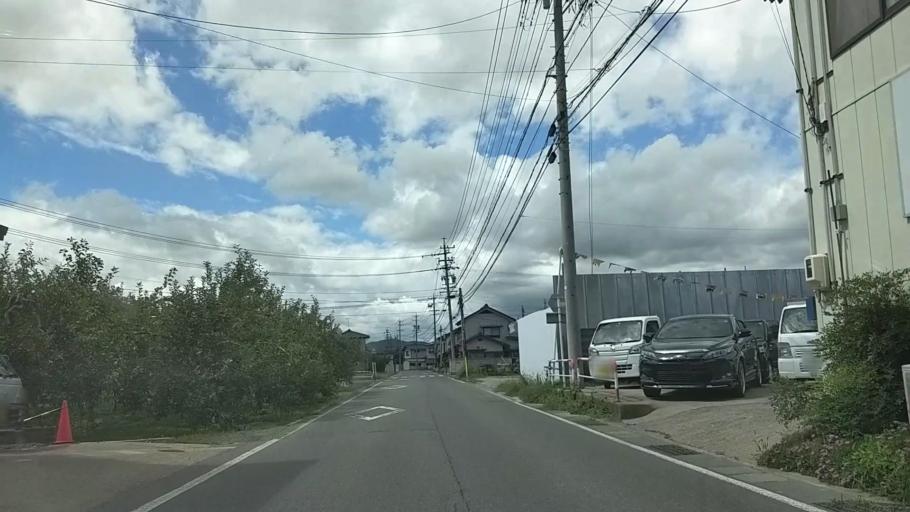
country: JP
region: Nagano
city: Nagano-shi
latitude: 36.6098
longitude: 138.2008
